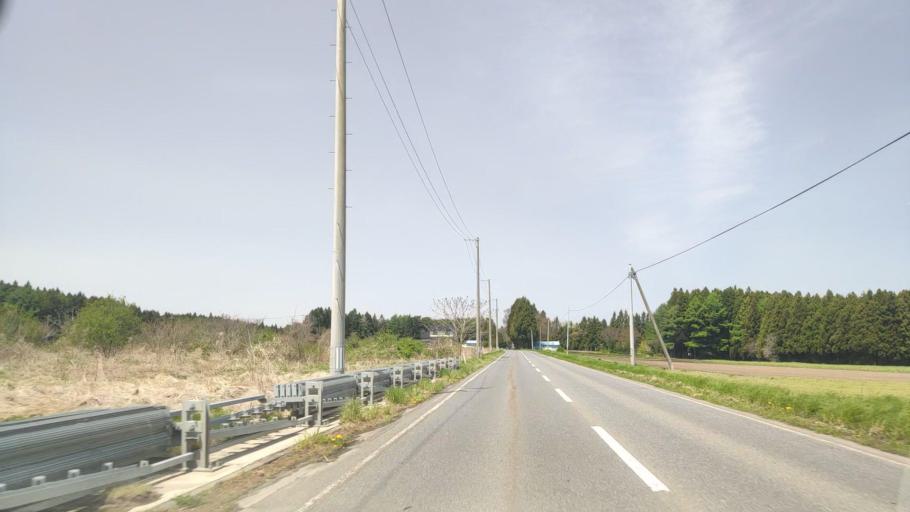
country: JP
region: Aomori
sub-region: Hachinohe Shi
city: Uchimaru
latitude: 40.5301
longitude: 141.4061
